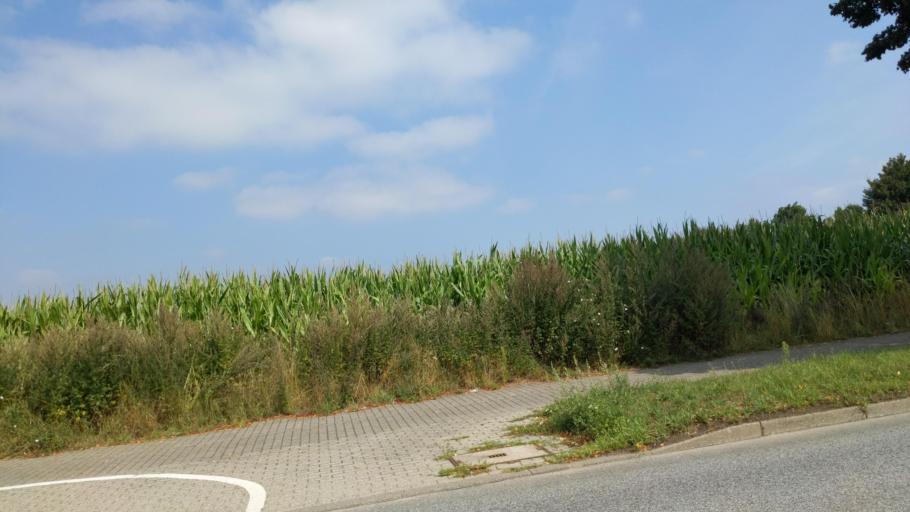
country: DE
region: Schleswig-Holstein
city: Stockelsdorf
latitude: 53.8695
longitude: 10.6298
